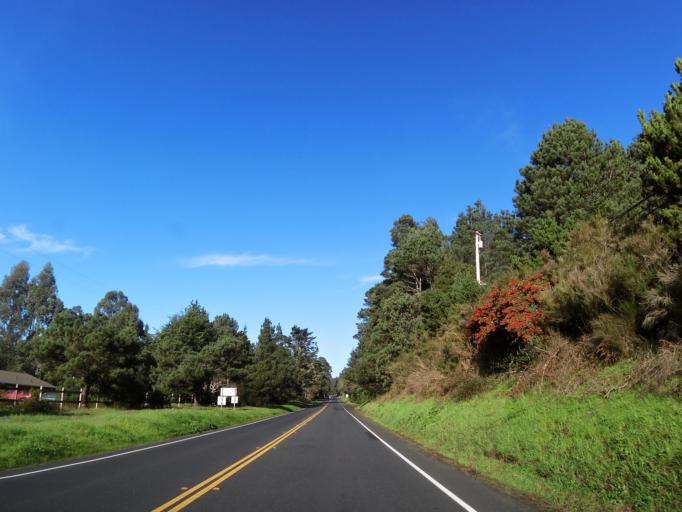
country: US
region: California
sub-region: Mendocino County
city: Fort Bragg
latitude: 39.3897
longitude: -123.8118
